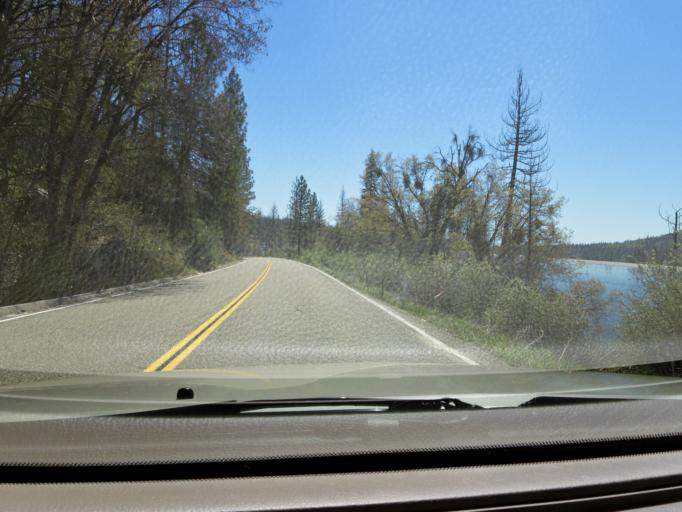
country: US
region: California
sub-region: Madera County
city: Oakhurst
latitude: 37.3004
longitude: -119.5274
